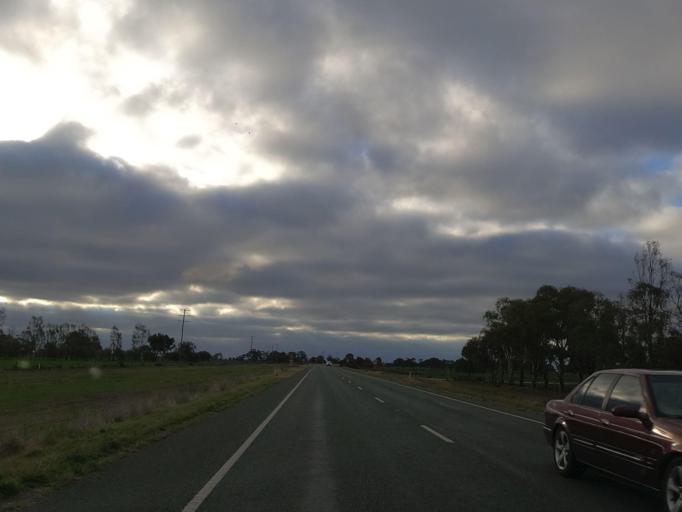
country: AU
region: Victoria
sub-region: Swan Hill
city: Swan Hill
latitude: -35.7077
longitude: 143.8818
